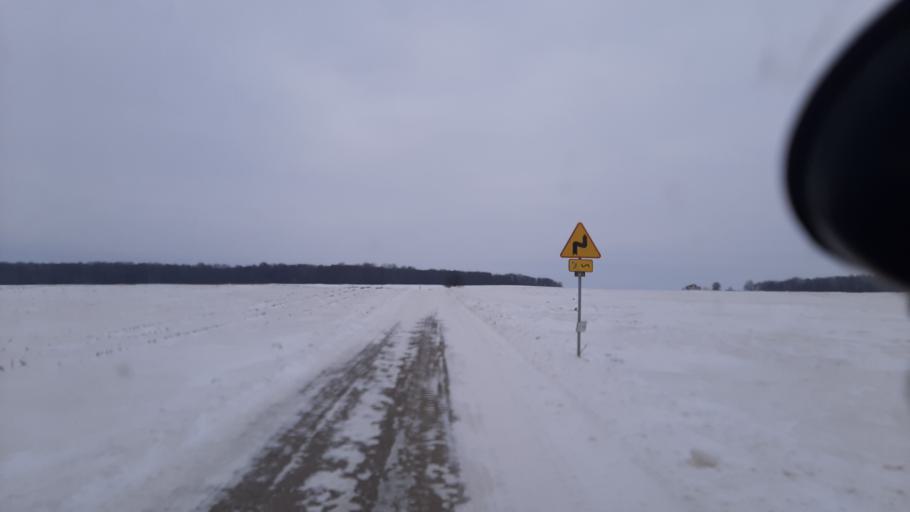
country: PL
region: Lublin Voivodeship
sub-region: Powiat lubelski
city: Garbow
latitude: 51.3227
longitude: 22.3106
